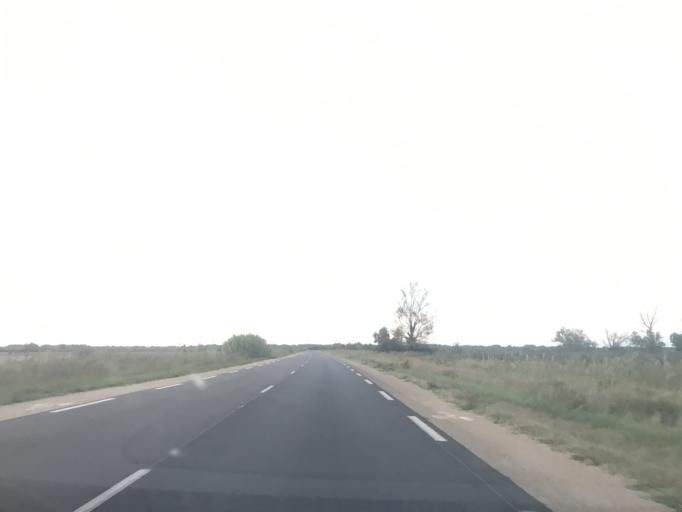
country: FR
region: Provence-Alpes-Cote d'Azur
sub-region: Departement des Bouches-du-Rhone
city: Saintes-Maries-de-la-Mer
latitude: 43.5332
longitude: 4.4004
